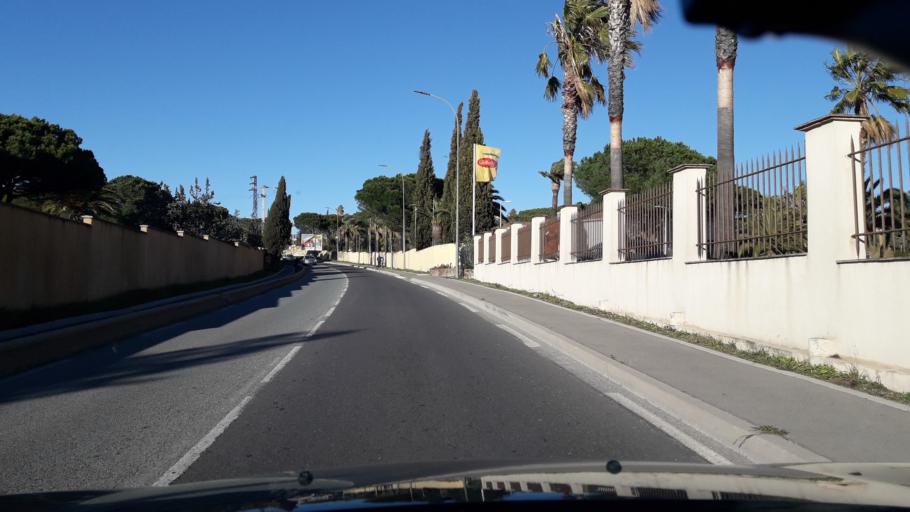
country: FR
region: Provence-Alpes-Cote d'Azur
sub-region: Departement du Var
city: Frejus
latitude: 43.4457
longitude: 6.7267
